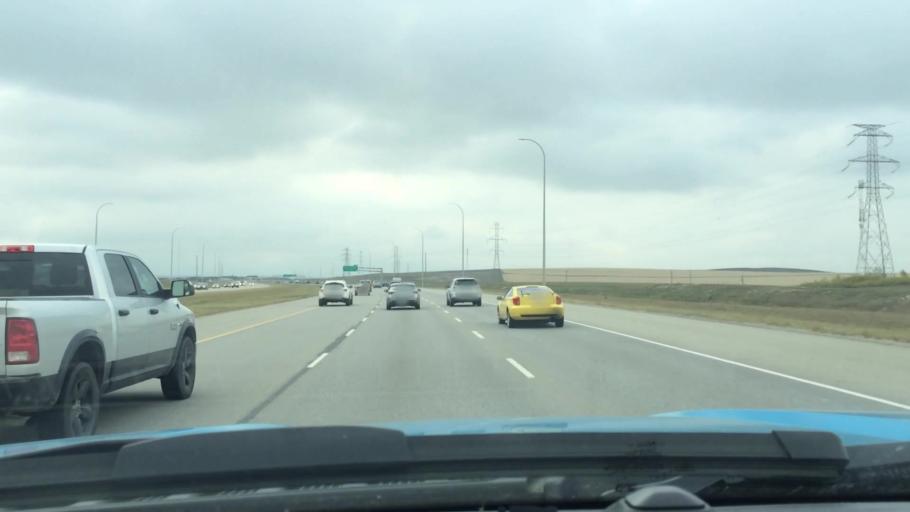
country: CA
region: Alberta
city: Airdrie
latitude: 51.1762
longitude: -114.0431
